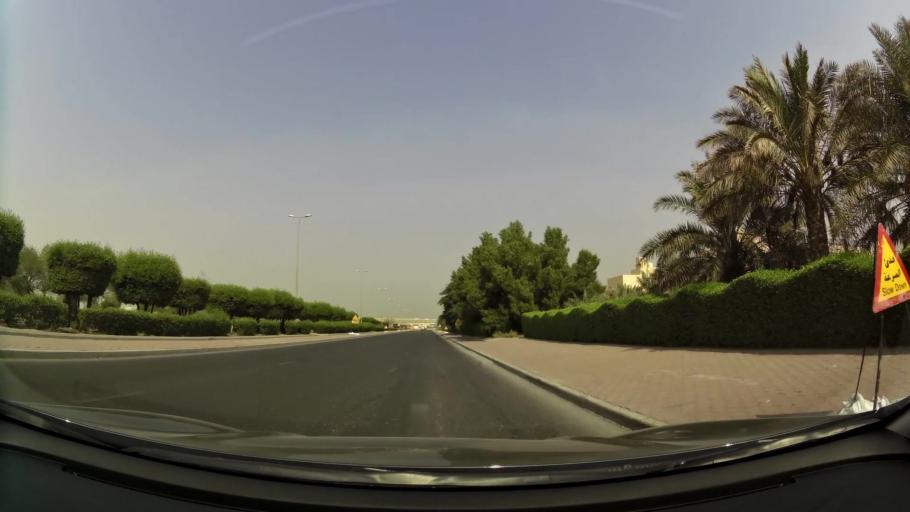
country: KW
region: Al Asimah
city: Ar Rabiyah
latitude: 29.3058
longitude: 47.8654
